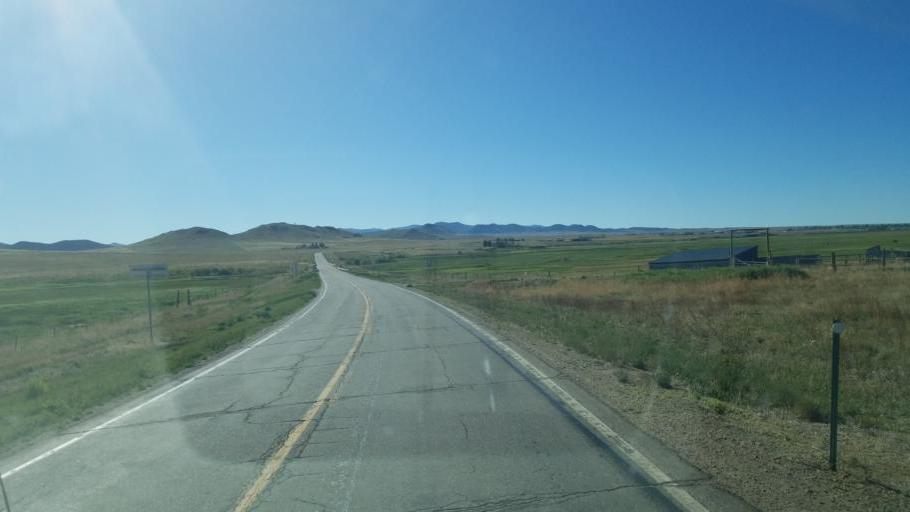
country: US
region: Colorado
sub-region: Custer County
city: Westcliffe
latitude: 38.1700
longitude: -105.5003
